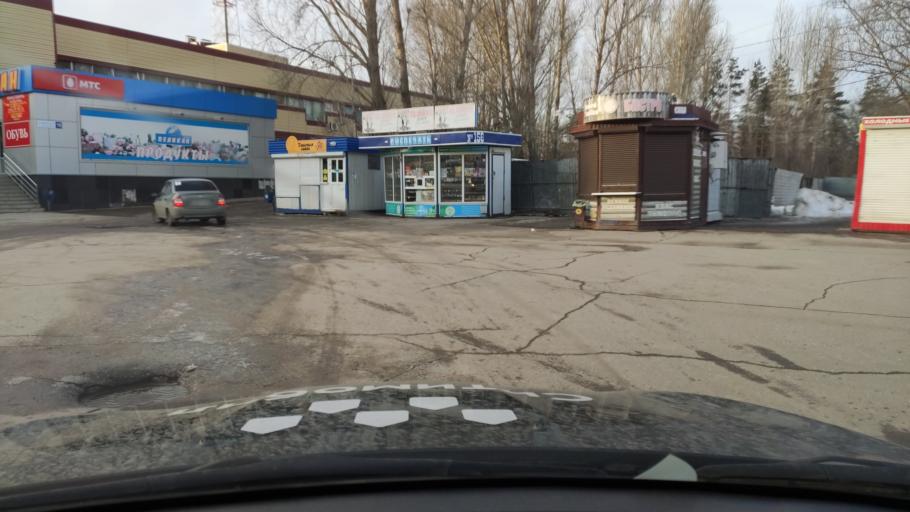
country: RU
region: Samara
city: Povolzhskiy
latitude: 53.5855
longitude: 49.7612
